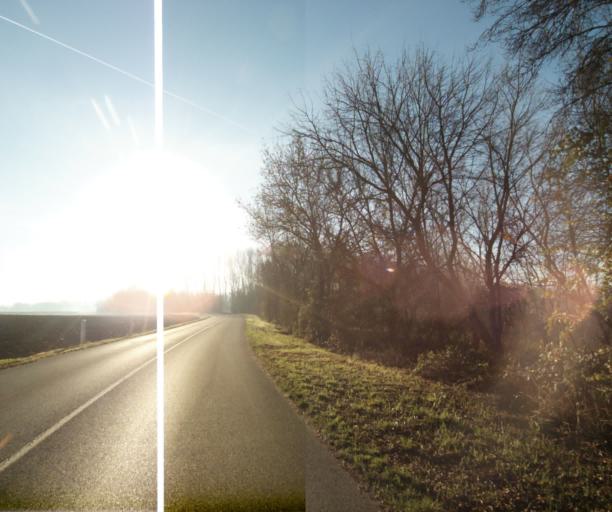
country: FR
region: Poitou-Charentes
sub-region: Departement de la Charente-Maritime
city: Cherac
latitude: 45.6939
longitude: -0.4759
